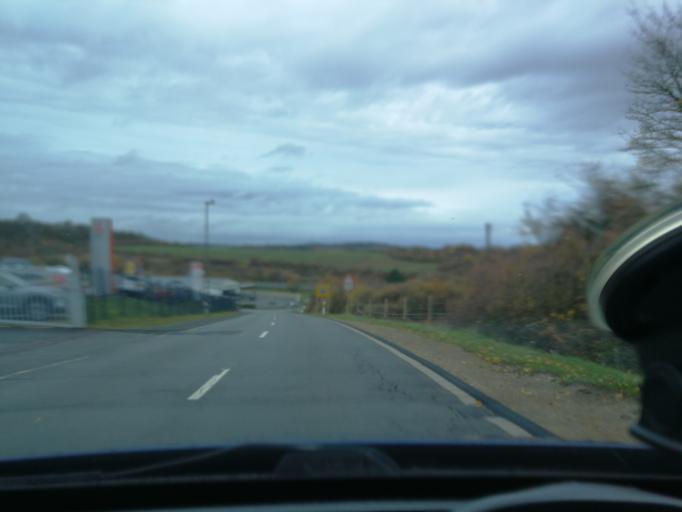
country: DE
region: Rheinland-Pfalz
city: Aach
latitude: 49.7717
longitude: 6.5925
